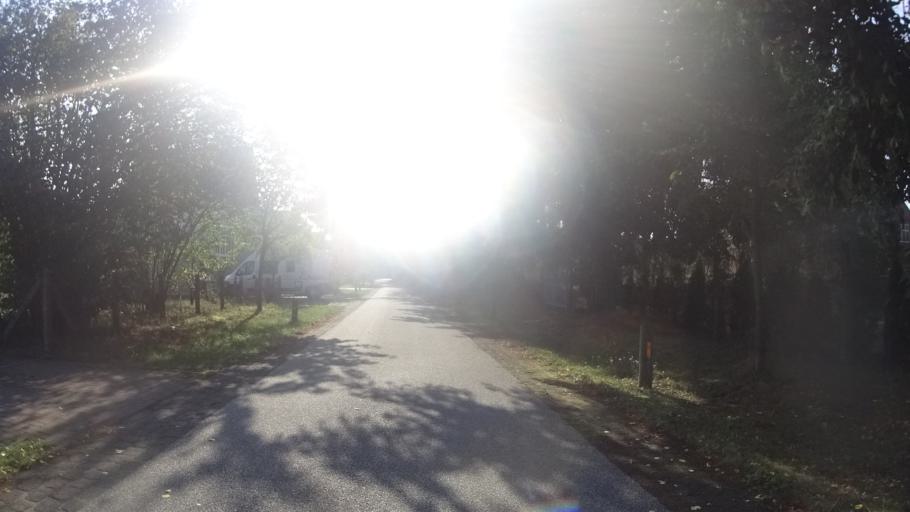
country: DE
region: Brandenburg
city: Cumlosen
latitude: 53.0262
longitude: 11.6763
